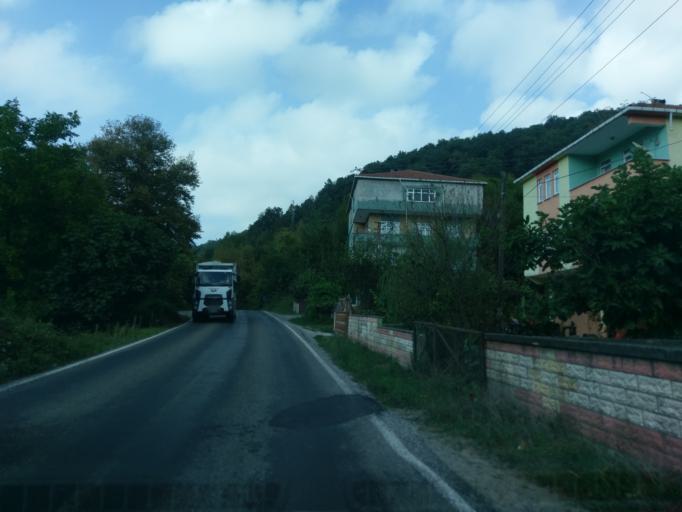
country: TR
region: Sinop
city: Helaldi
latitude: 41.9274
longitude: 34.4164
